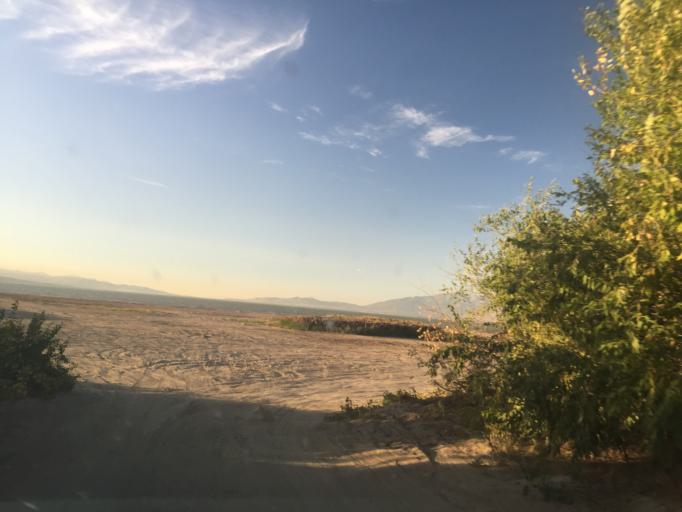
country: US
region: Utah
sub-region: Utah County
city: Benjamin
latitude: 40.1671
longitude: -111.7480
